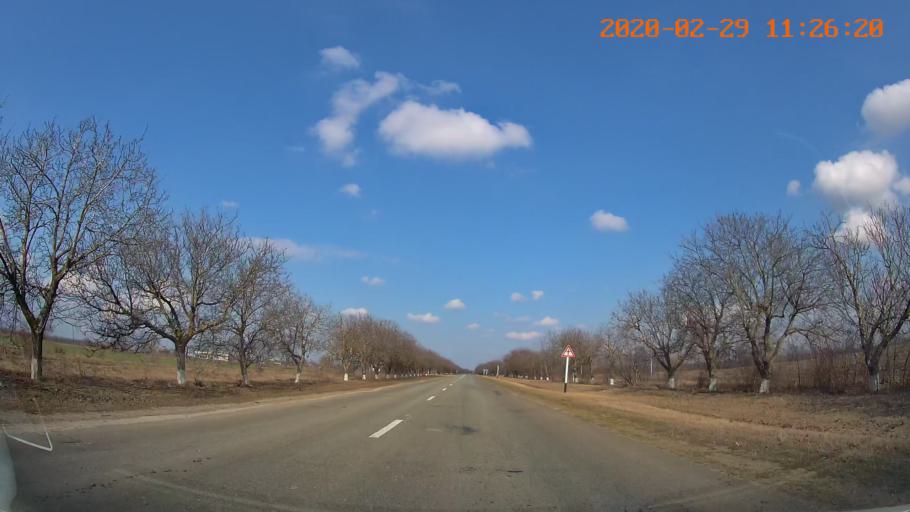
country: MD
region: Telenesti
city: Cocieri
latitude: 47.4517
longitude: 29.1465
